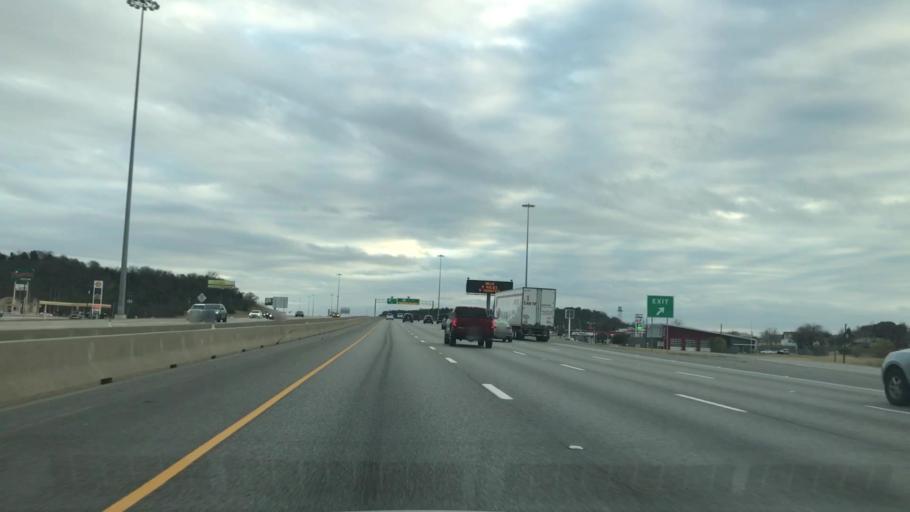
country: US
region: Texas
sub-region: Dallas County
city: Cockrell Hill
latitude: 32.7399
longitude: -96.9194
